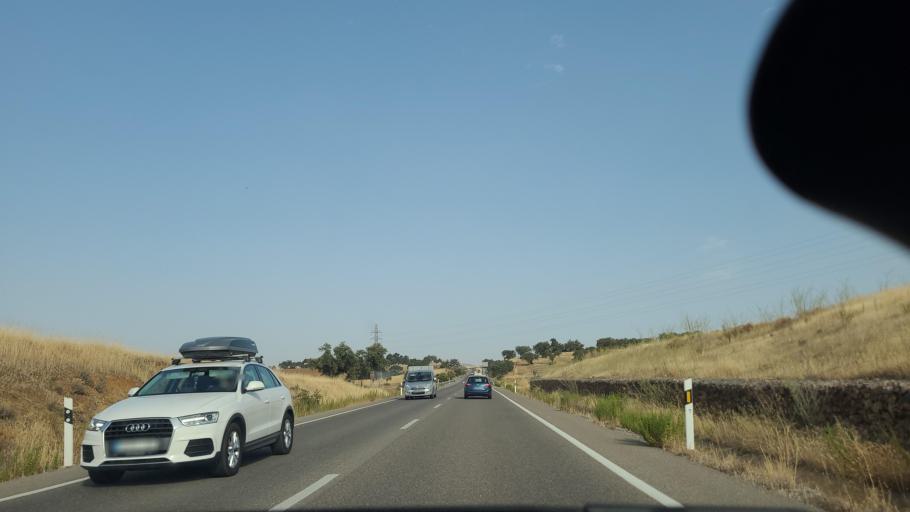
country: ES
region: Andalusia
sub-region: Province of Cordoba
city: Belmez
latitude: 38.2831
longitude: -5.2120
